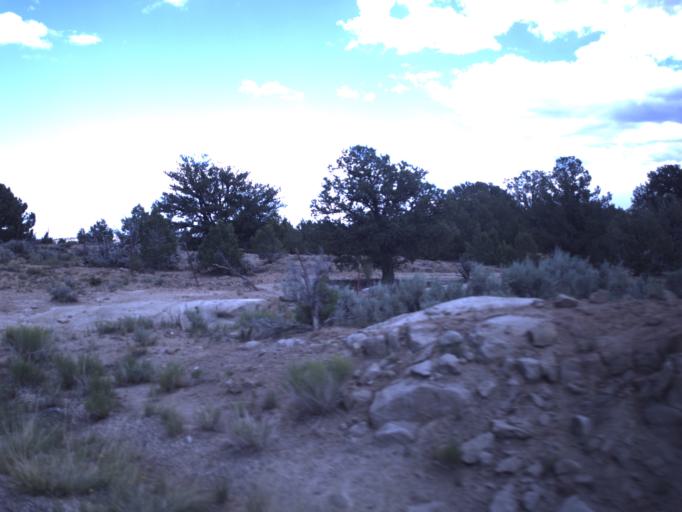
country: US
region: Utah
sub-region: Duchesne County
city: Duchesne
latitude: 40.2454
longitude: -110.7124
